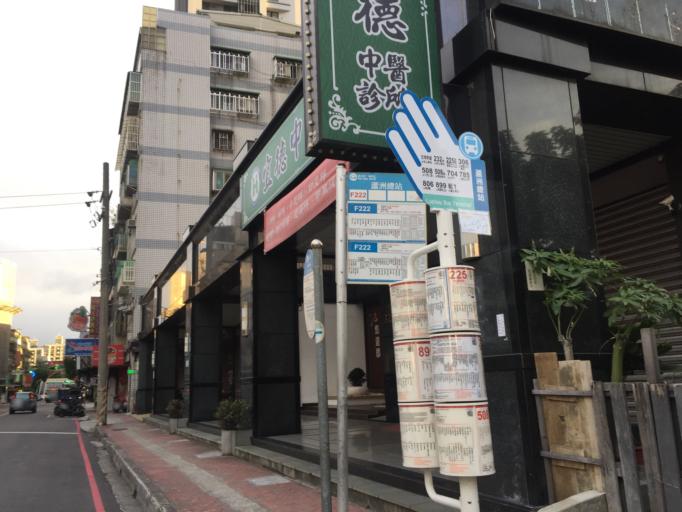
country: TW
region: Taipei
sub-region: Taipei
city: Banqiao
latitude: 25.0890
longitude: 121.4660
